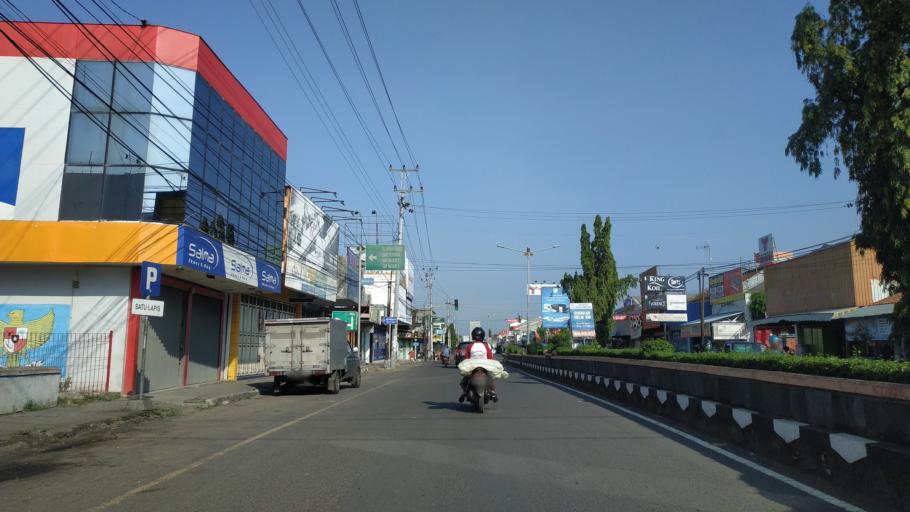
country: ID
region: Central Java
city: Pemalang
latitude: -6.8904
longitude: 109.3892
